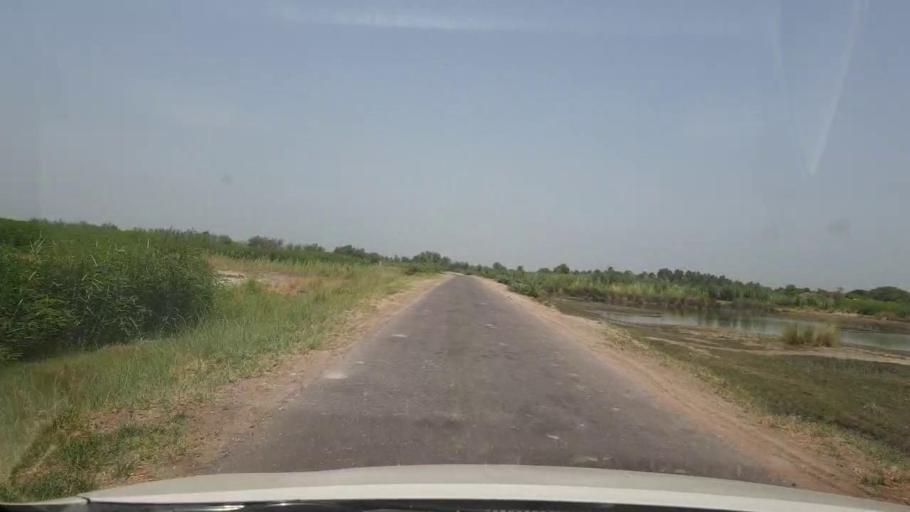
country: PK
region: Sindh
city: Bozdar
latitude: 27.2547
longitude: 68.6389
